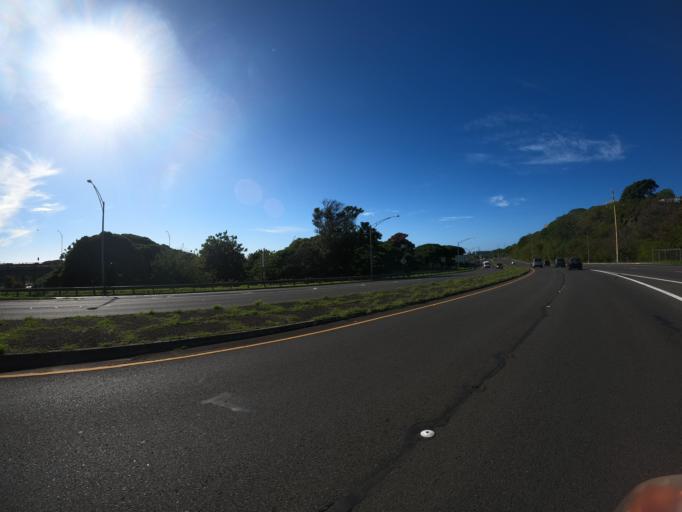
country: US
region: Hawaii
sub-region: Honolulu County
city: Halawa Heights
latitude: 21.3486
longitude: -157.8967
